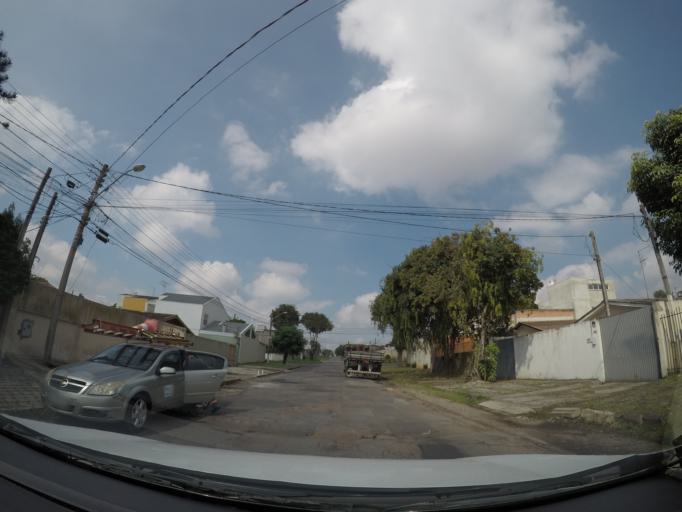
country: BR
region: Parana
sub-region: Curitiba
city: Curitiba
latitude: -25.4787
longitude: -49.2597
